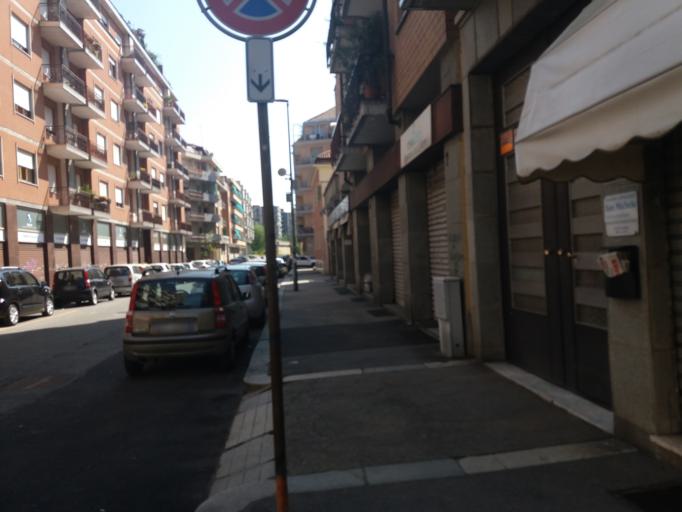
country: IT
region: Piedmont
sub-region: Provincia di Torino
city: Lesna
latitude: 45.0711
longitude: 7.6309
